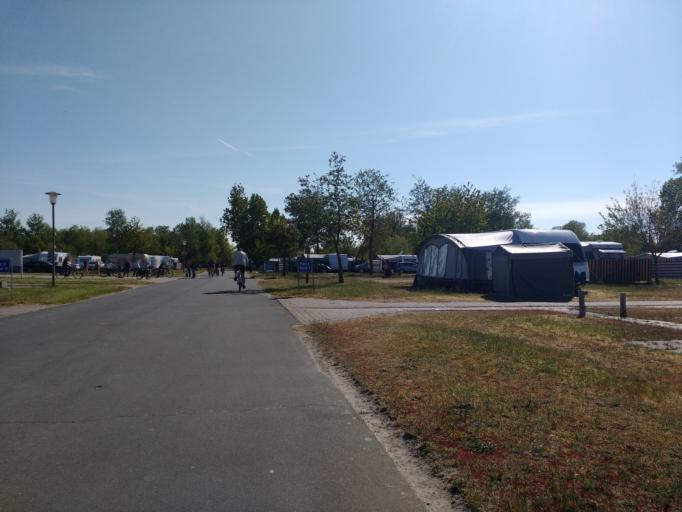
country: DE
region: Lower Saxony
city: Schillig
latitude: 53.6960
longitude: 8.0224
